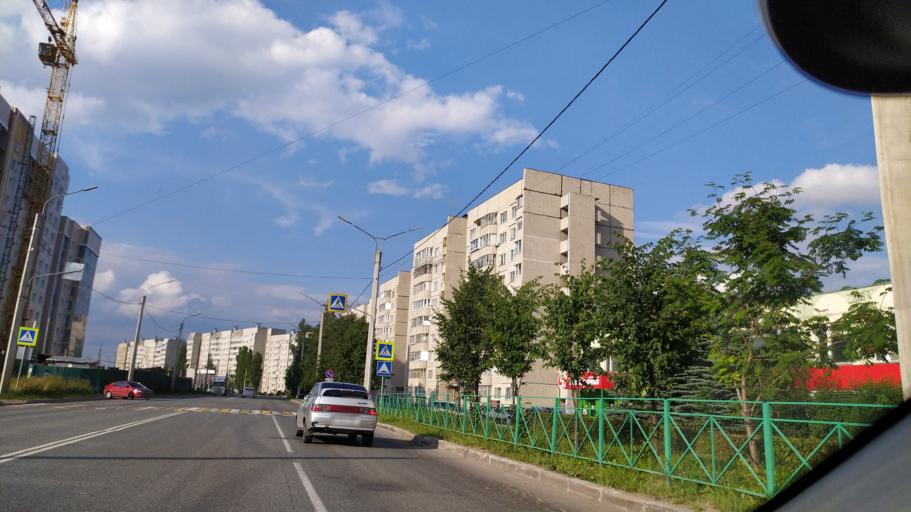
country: RU
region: Chuvashia
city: Novocheboksarsk
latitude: 56.1153
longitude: 47.4421
